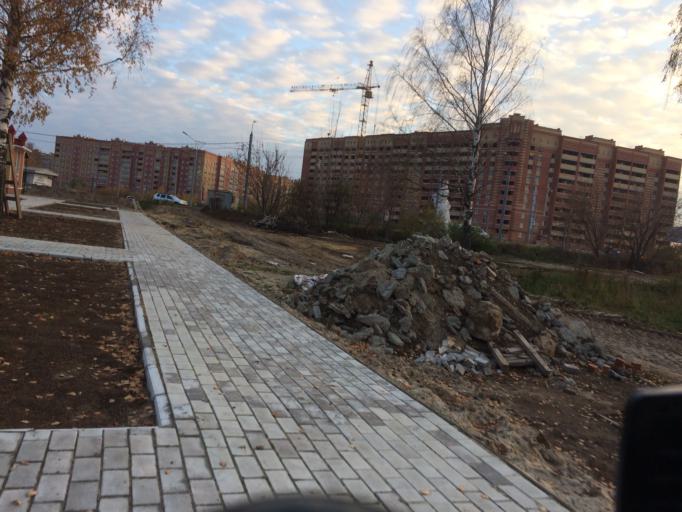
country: RU
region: Mariy-El
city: Yoshkar-Ola
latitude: 56.6445
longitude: 47.9255
